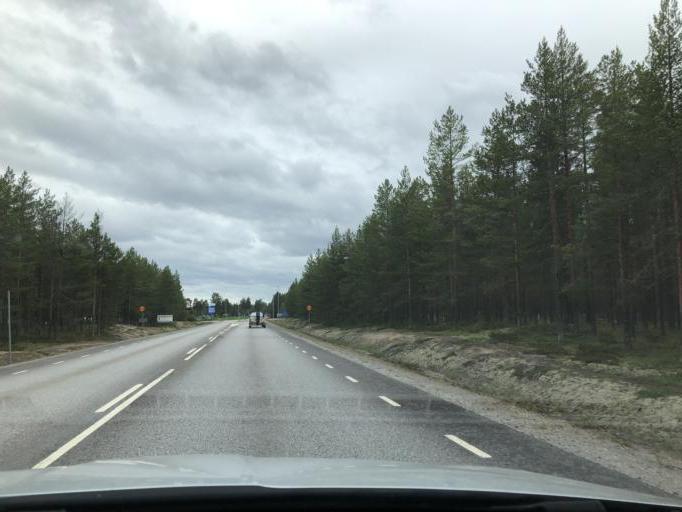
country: SE
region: Norrbotten
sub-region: Pitea Kommun
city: Pitea
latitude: 65.2395
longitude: 21.5280
